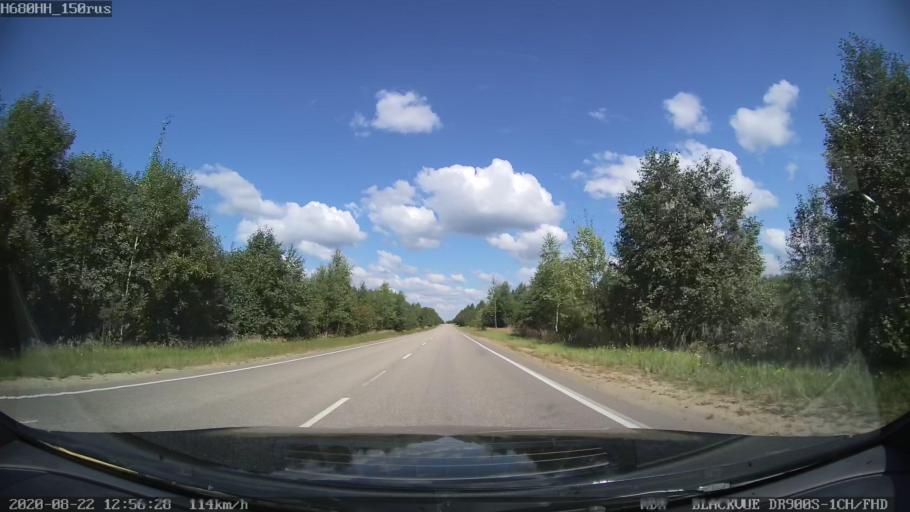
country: RU
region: Tverskaya
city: Rameshki
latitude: 57.5567
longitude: 36.3169
